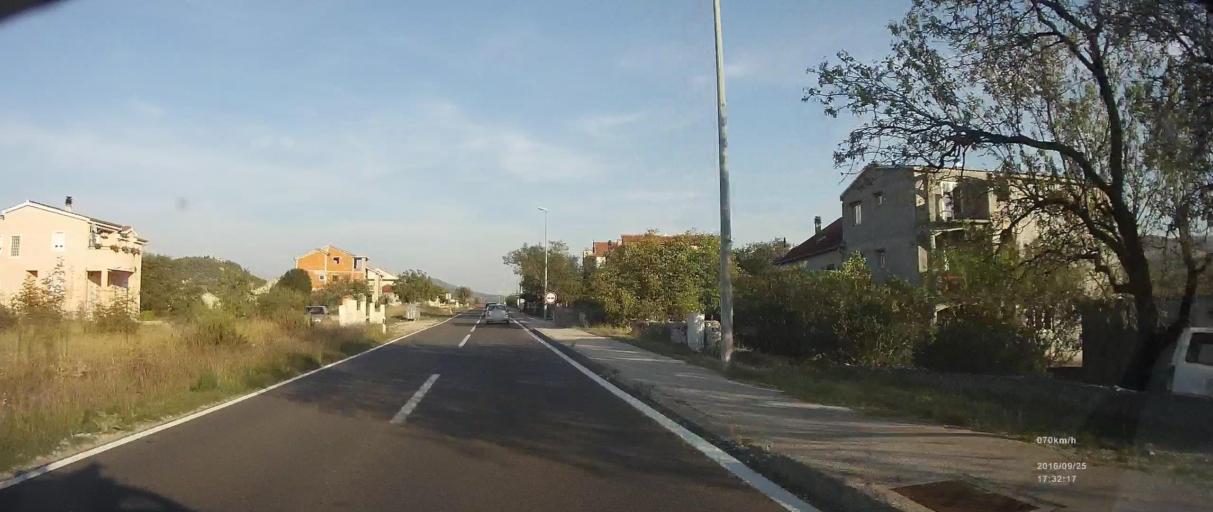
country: HR
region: Sibensko-Kniniska
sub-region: Grad Sibenik
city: Brodarica
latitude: 43.6752
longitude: 16.0004
